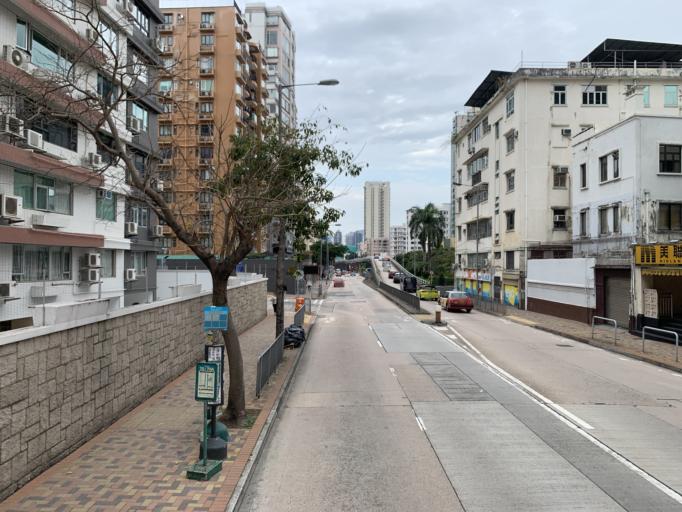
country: HK
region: Kowloon City
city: Kowloon
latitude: 22.3272
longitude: 114.1837
